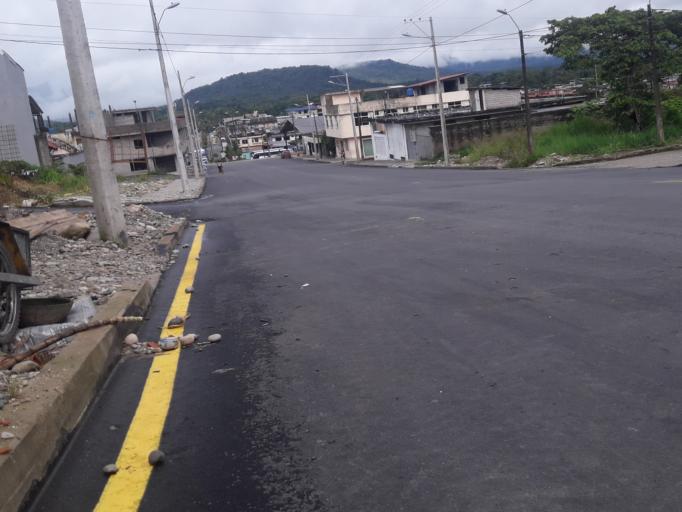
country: EC
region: Napo
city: Tena
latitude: -0.9993
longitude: -77.8082
